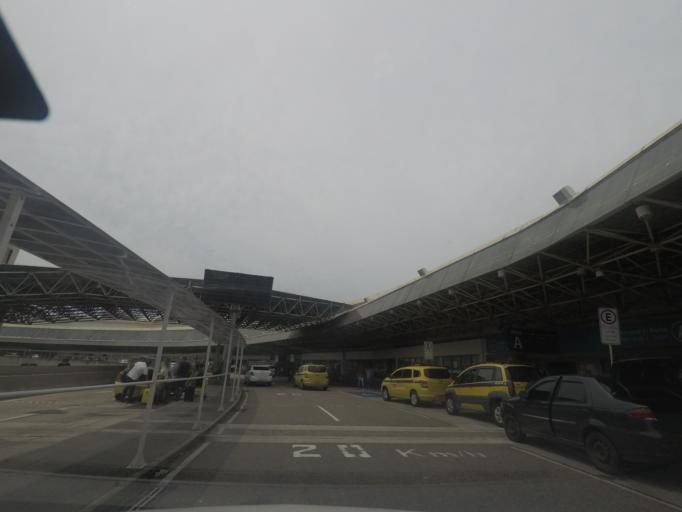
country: BR
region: Rio de Janeiro
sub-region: Duque De Caxias
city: Duque de Caxias
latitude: -22.8139
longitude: -43.2469
